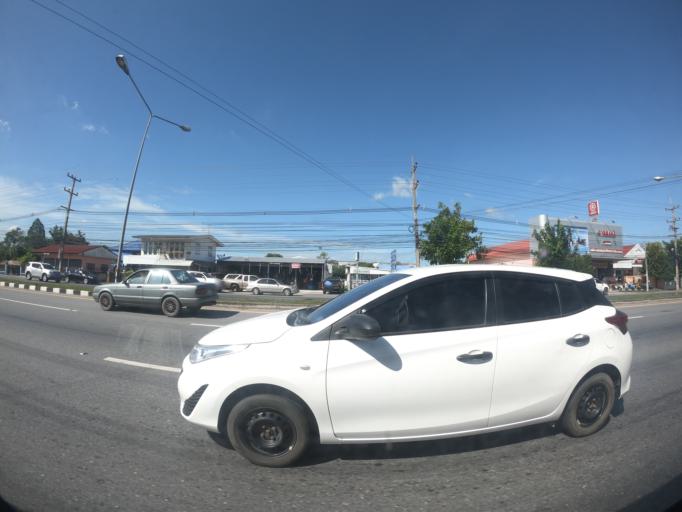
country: TH
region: Nakhon Nayok
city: Ban Na
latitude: 14.2584
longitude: 101.0761
